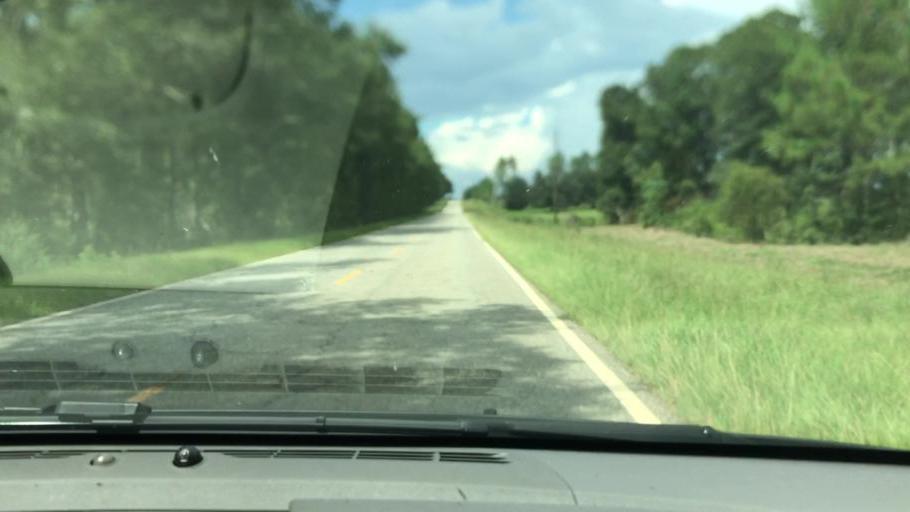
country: US
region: Georgia
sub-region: Early County
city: Blakely
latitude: 31.2663
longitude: -84.9907
